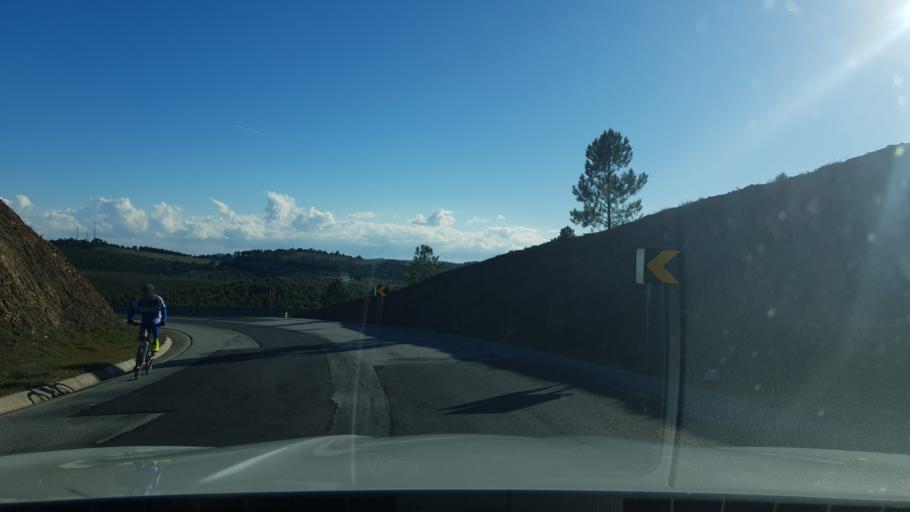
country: PT
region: Braganca
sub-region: Freixo de Espada A Cinta
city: Freixo de Espada a Cinta
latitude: 41.1295
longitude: -6.8192
